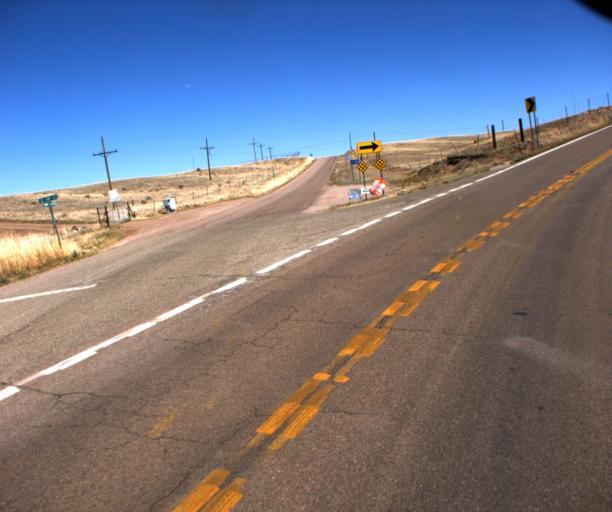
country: US
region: Arizona
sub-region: Cochise County
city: Huachuca City
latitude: 31.6735
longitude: -110.6116
